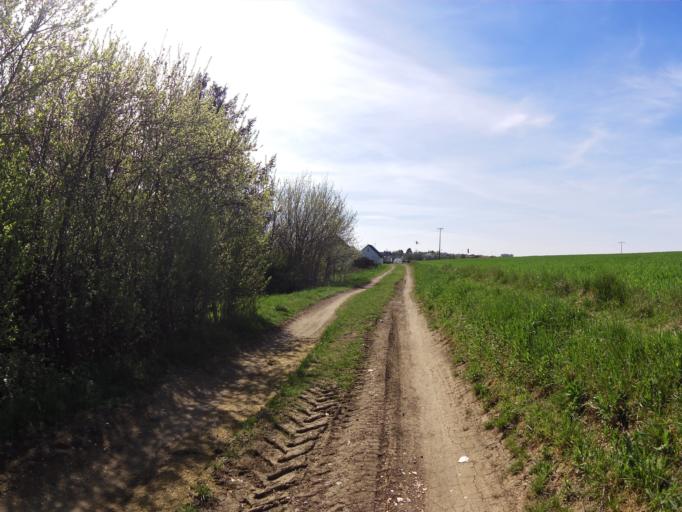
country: DE
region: Bavaria
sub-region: Regierungsbezirk Unterfranken
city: Rimpar
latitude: 49.8503
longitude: 9.9782
